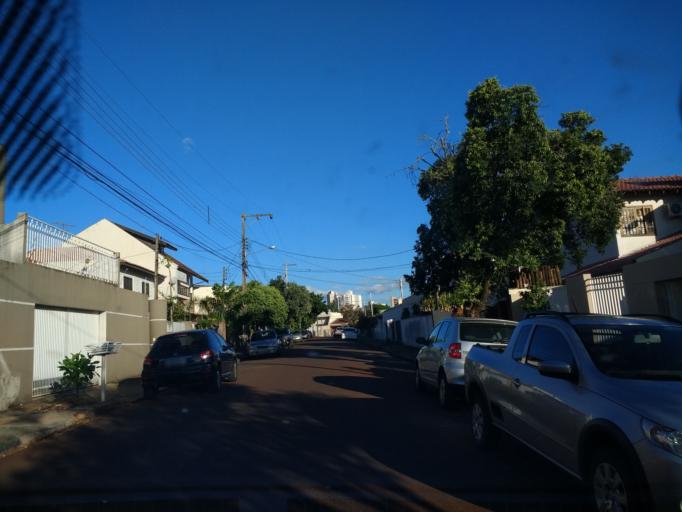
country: BR
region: Parana
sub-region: Londrina
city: Londrina
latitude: -23.3295
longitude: -51.1603
